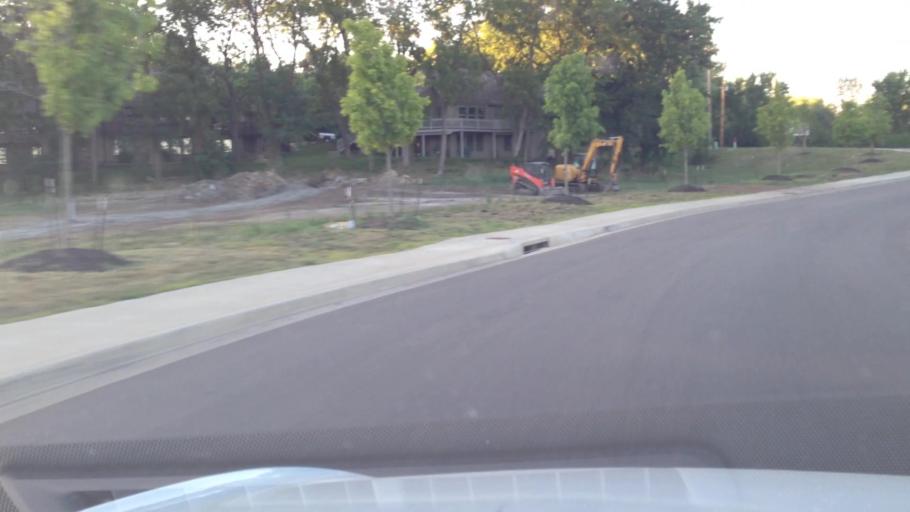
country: US
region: Kansas
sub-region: Douglas County
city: Lawrence
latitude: 38.9558
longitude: -95.2937
